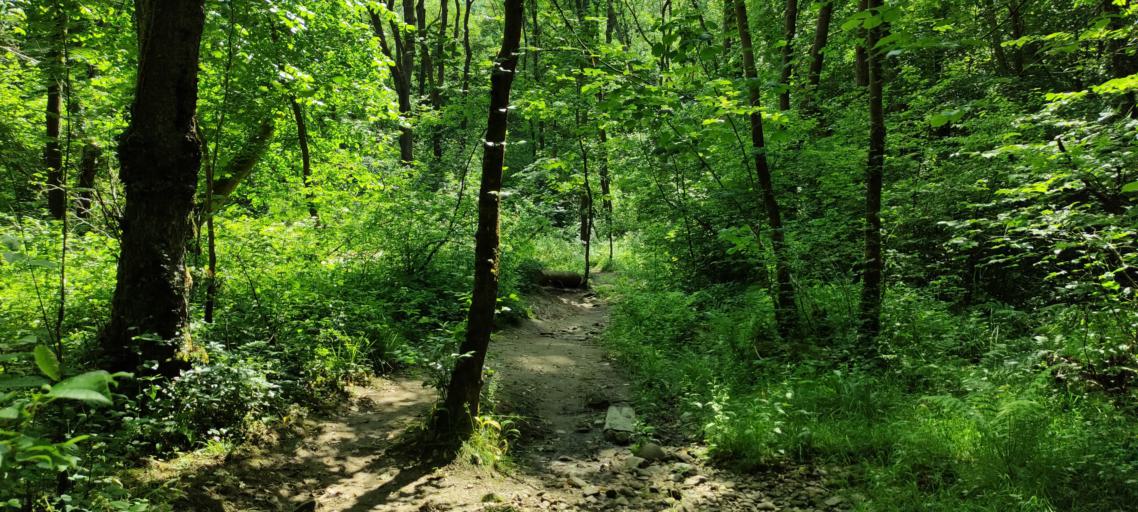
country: GB
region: England
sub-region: North Yorkshire
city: Bedale
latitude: 54.1897
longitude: -1.6397
